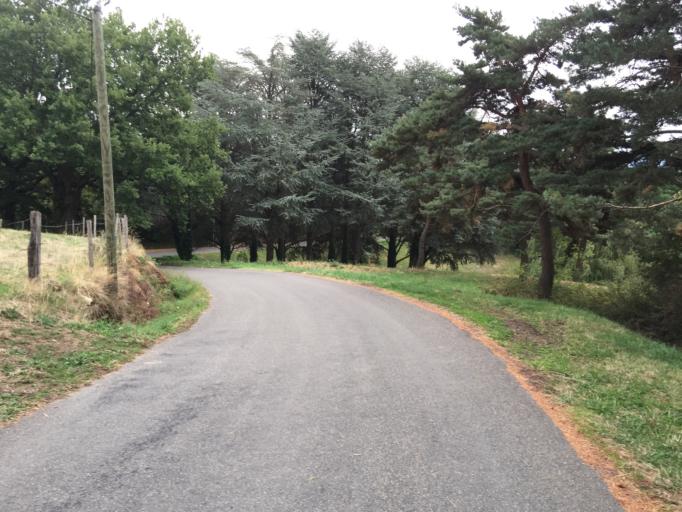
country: FR
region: Rhone-Alpes
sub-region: Departement de la Loire
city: Sorbiers
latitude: 45.4928
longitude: 4.4802
